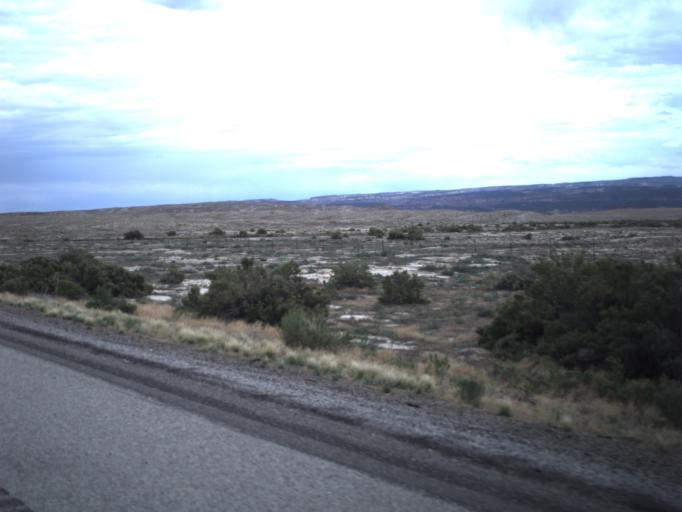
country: US
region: Utah
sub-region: Grand County
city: Moab
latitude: 38.9968
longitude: -109.3253
